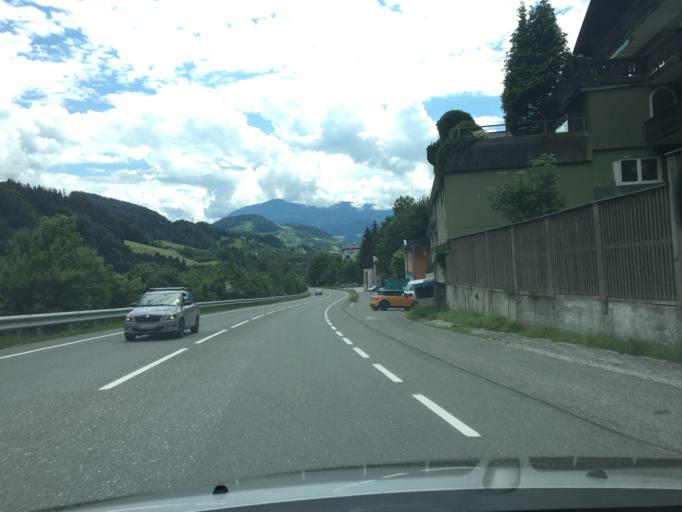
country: AT
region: Salzburg
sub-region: Politischer Bezirk Sankt Johann im Pongau
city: Werfen
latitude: 47.4788
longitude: 13.1881
